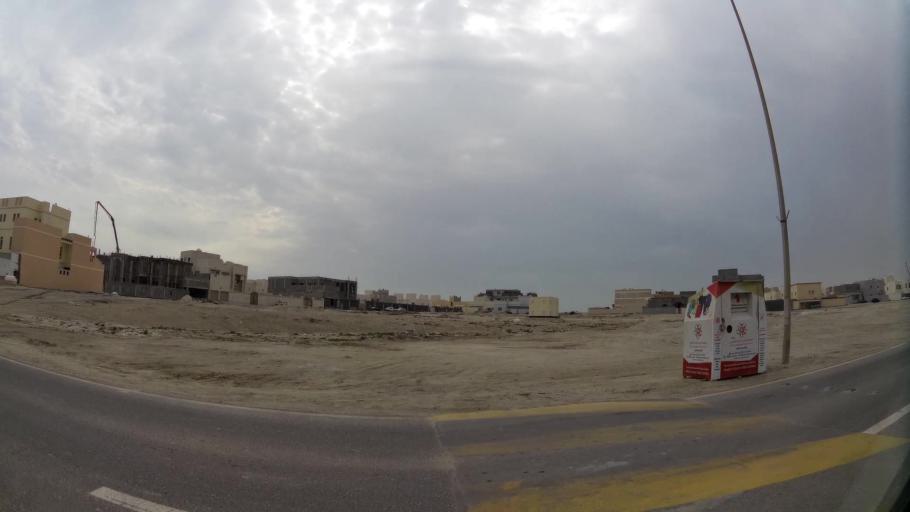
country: BH
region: Northern
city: Ar Rifa'
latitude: 26.0537
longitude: 50.6182
